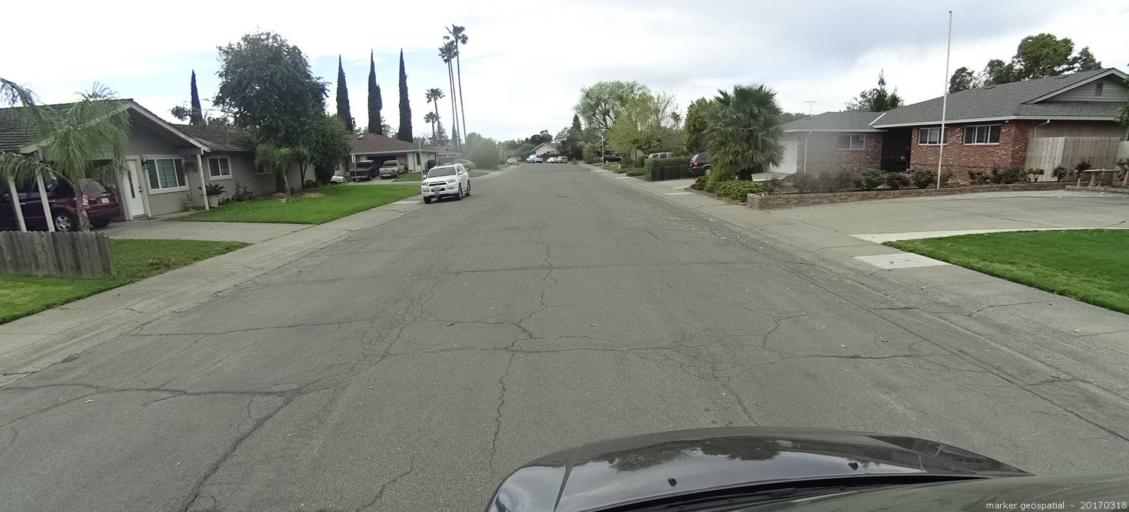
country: US
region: California
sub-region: Sacramento County
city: Parkway
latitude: 38.4800
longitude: -121.4381
